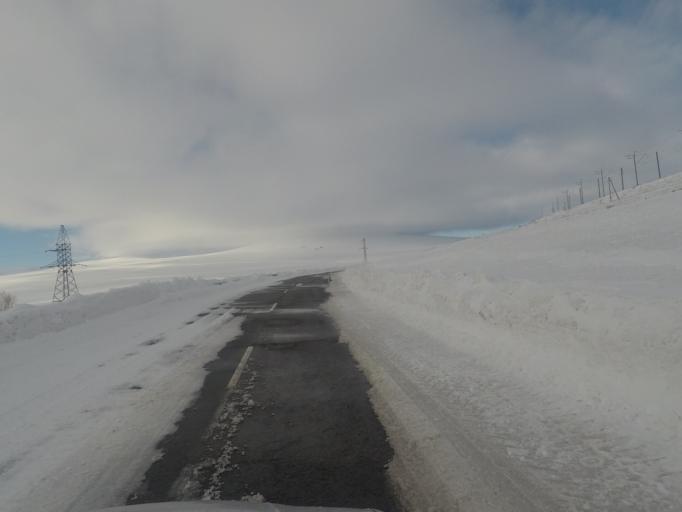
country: GE
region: Kvemo Kartli
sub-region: Tsalka
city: Tsalka
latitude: 41.4773
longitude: 43.8504
